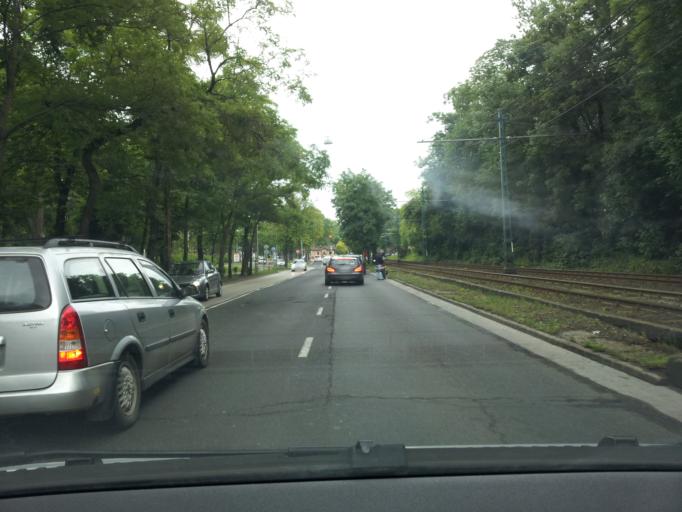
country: HU
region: Budapest
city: Budapest XII. keruelet
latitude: 47.5113
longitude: 19.0068
